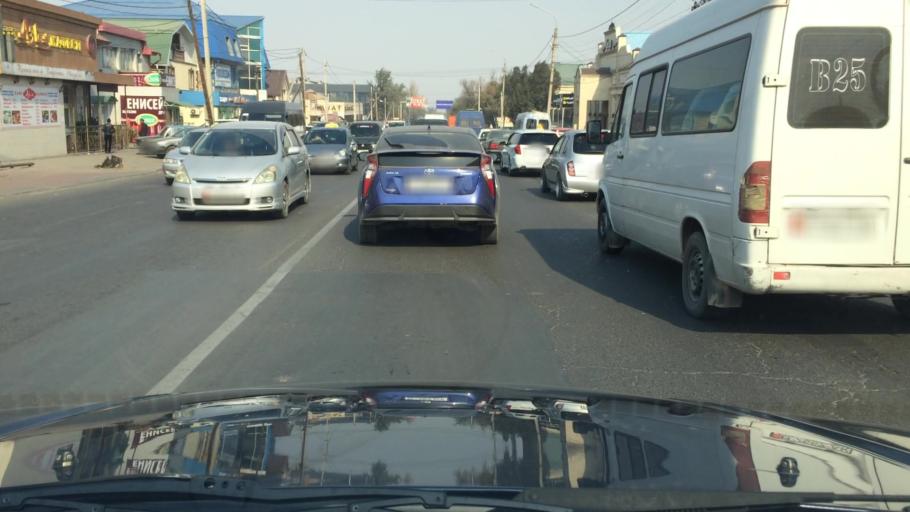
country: KG
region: Chuy
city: Lebedinovka
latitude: 42.8802
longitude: 74.6373
